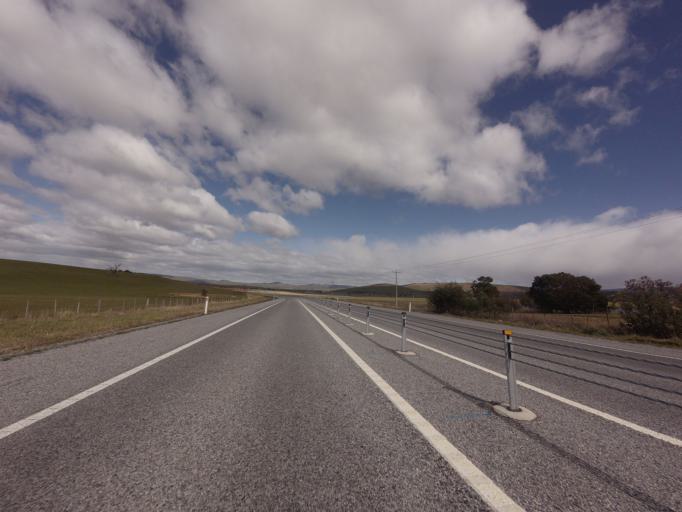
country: AU
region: Tasmania
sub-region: Northern Midlands
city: Evandale
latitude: -42.0871
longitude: 147.4544
